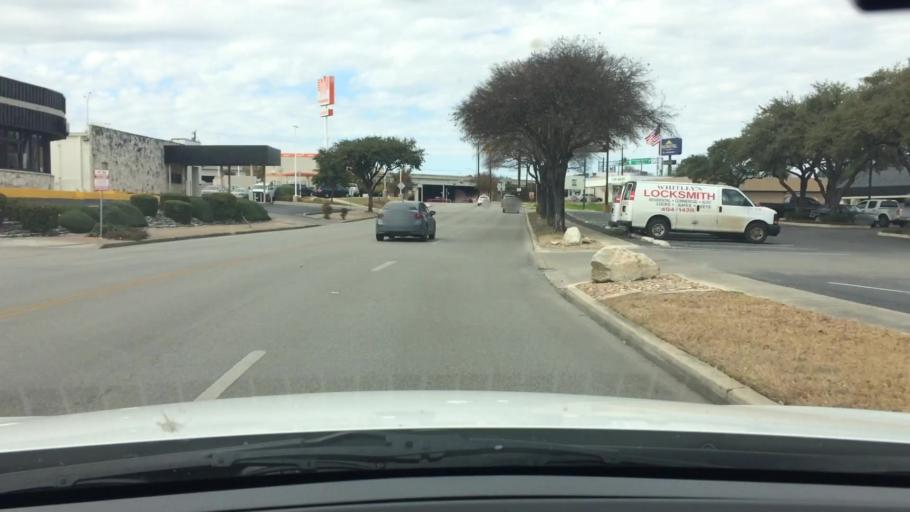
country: US
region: Texas
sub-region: Bexar County
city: Hollywood Park
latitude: 29.5791
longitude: -98.4752
